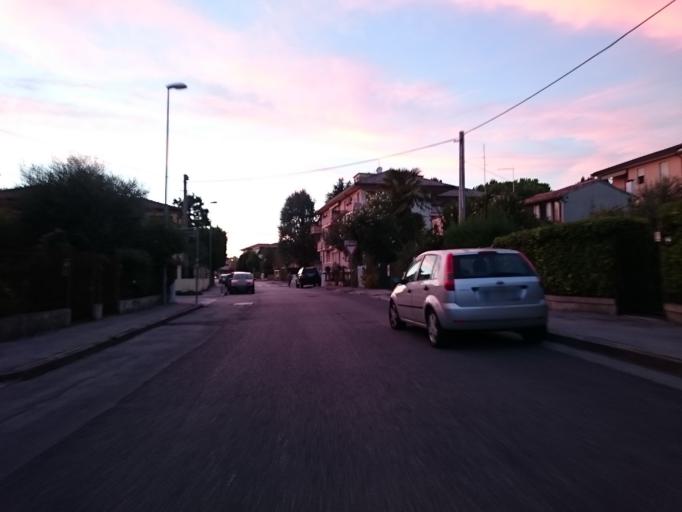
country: IT
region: Veneto
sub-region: Provincia di Padova
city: Padova
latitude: 45.3859
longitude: 11.8954
